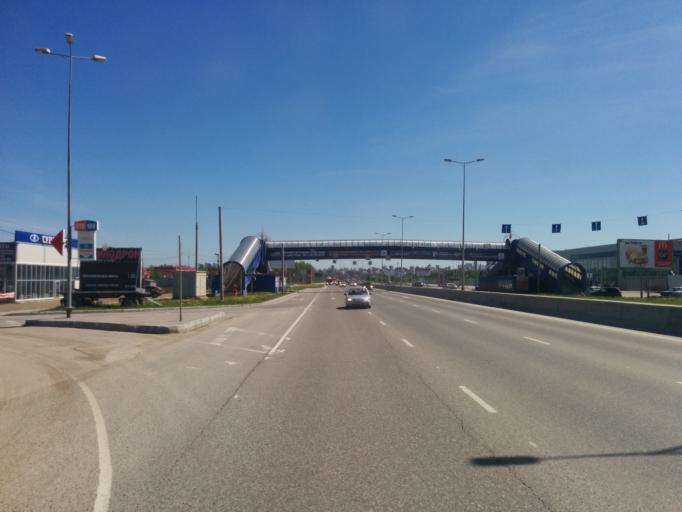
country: RU
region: Perm
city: Perm
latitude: 58.0357
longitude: 56.1989
